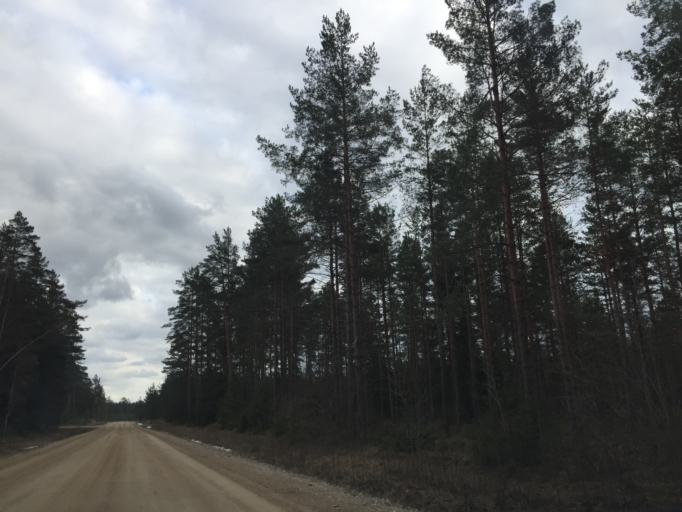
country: LV
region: Jaunjelgava
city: Jaunjelgava
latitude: 56.5844
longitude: 25.0019
